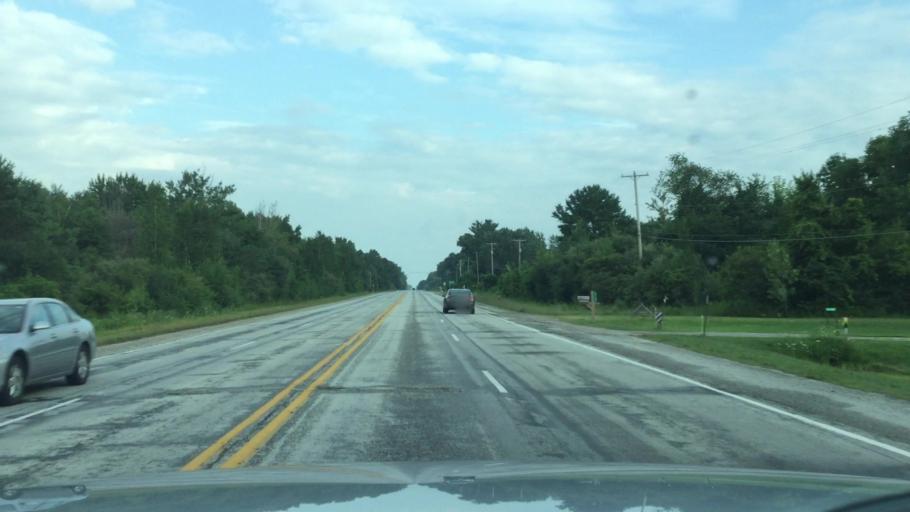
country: US
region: Michigan
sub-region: Saginaw County
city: Birch Run
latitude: 43.2965
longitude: -83.8044
